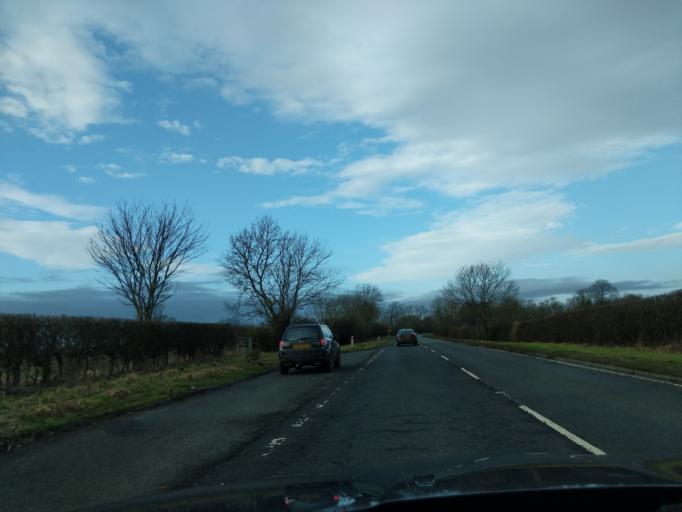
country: GB
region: England
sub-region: Northumberland
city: Darras Hall
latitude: 55.0684
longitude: -1.7877
